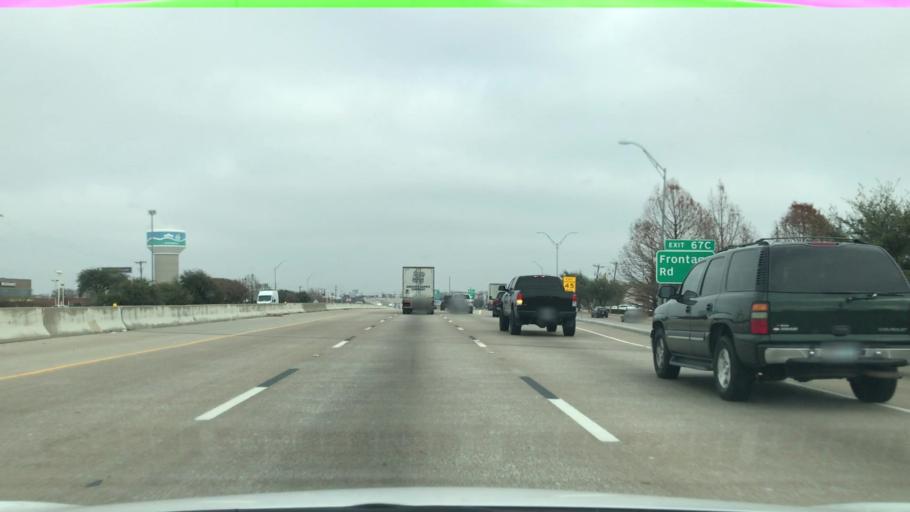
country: US
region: Texas
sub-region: Rockwall County
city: Rockwall
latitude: 32.8971
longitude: -96.4696
